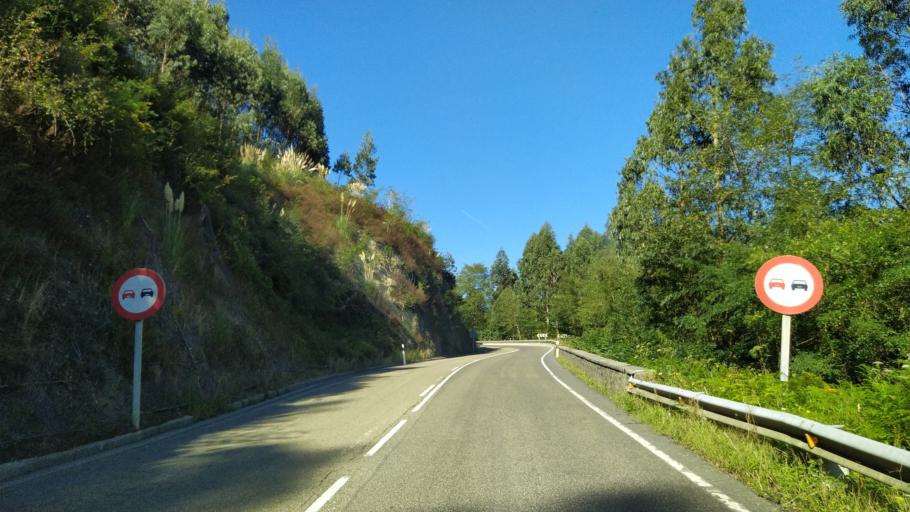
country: ES
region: Cantabria
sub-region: Provincia de Cantabria
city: Liendo
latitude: 43.3821
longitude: -3.3227
